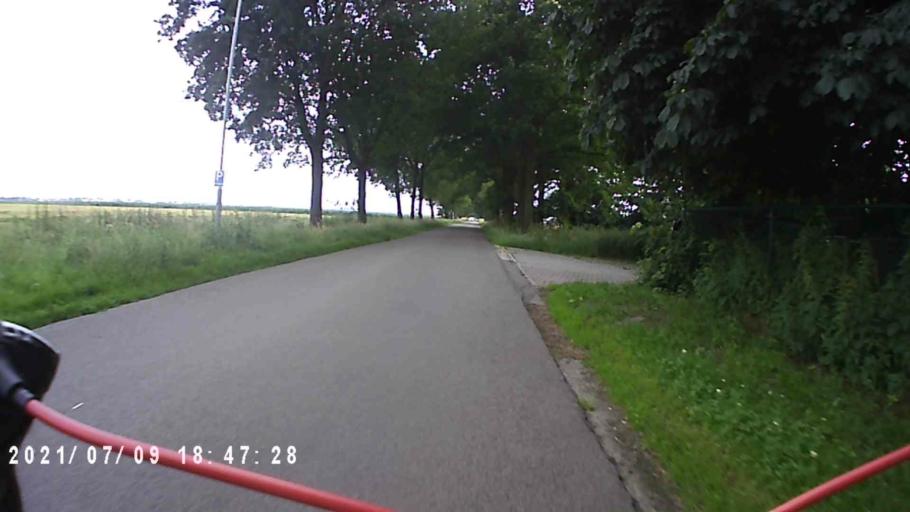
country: NL
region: Groningen
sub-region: Gemeente Veendam
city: Veendam
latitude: 53.0697
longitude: 6.9169
